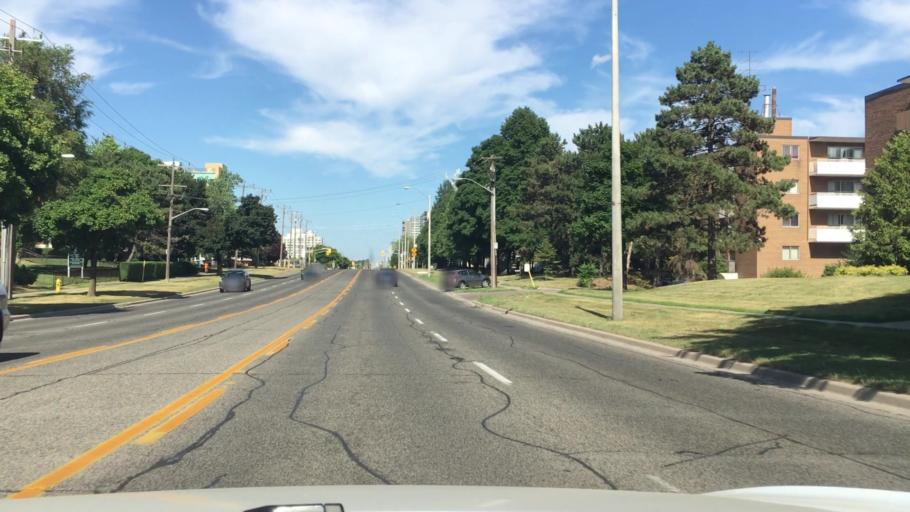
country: CA
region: Ontario
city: Scarborough
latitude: 43.7814
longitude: -79.2965
